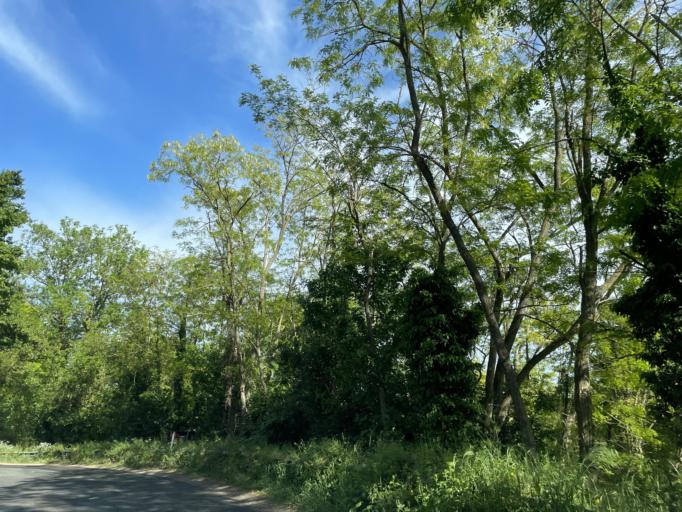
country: FR
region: Ile-de-France
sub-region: Departement de Seine-et-Marne
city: Charny
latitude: 48.9492
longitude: 2.7812
